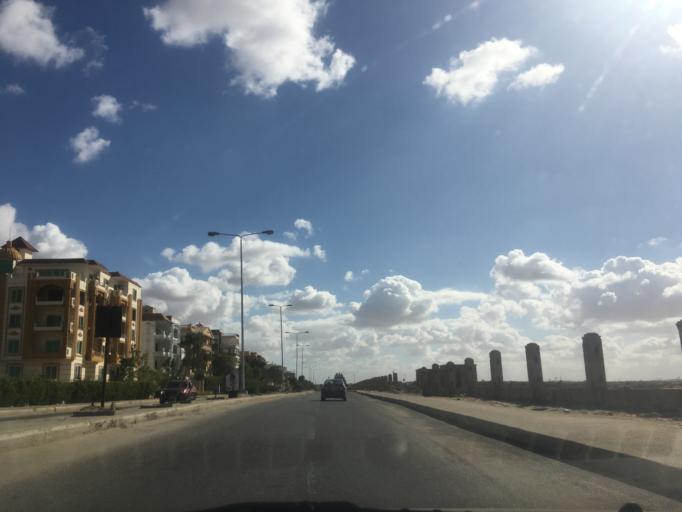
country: EG
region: Al Jizah
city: Madinat Sittah Uktubar
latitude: 30.0018
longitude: 30.9729
